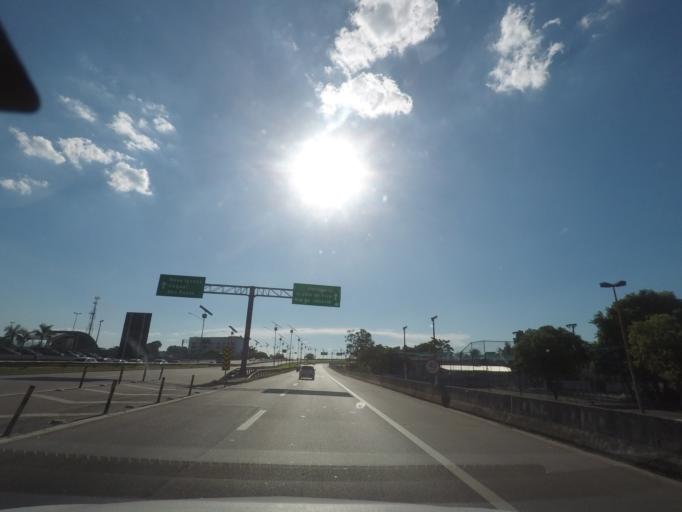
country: BR
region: Rio de Janeiro
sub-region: Duque De Caxias
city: Duque de Caxias
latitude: -22.6716
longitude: -43.2795
